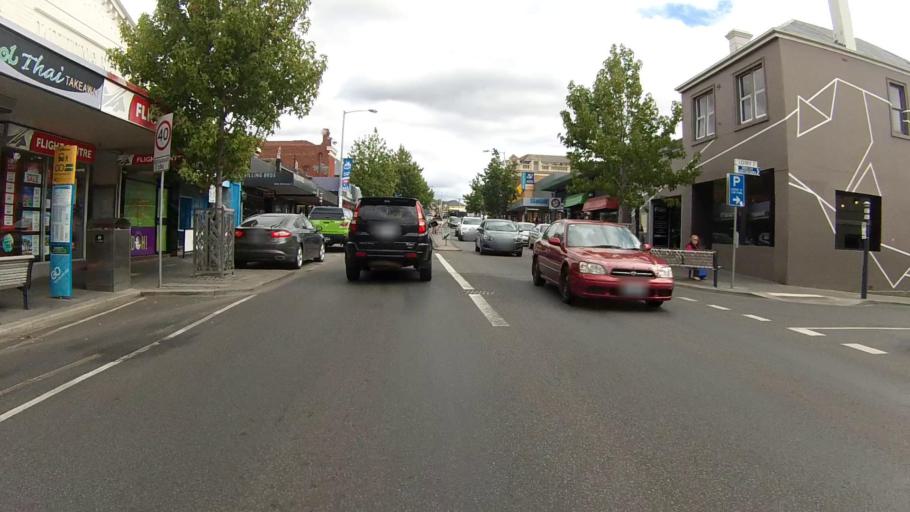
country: AU
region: Tasmania
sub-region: Hobart
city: Hobart
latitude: -42.8734
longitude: 147.3156
